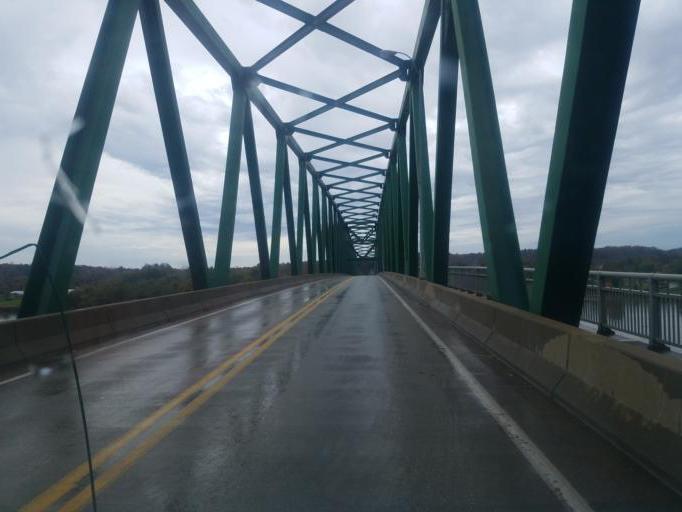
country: US
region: Ohio
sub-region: Washington County
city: Marietta
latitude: 39.4105
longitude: -81.4481
